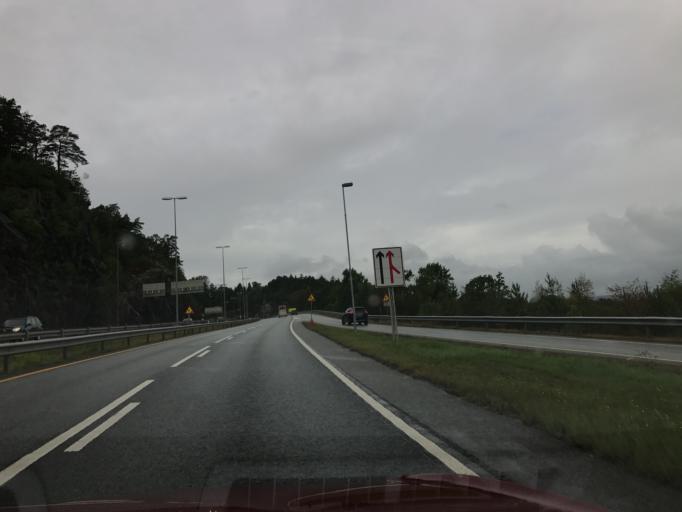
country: NO
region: Vest-Agder
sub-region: Kristiansand
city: Justvik
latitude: 58.1612
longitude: 8.0757
